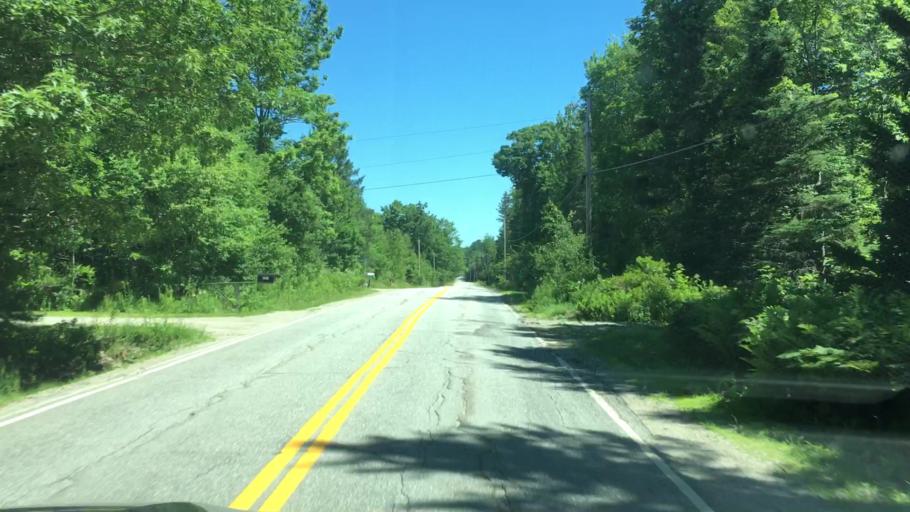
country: US
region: Maine
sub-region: Hancock County
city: Penobscot
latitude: 44.5014
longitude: -68.6801
